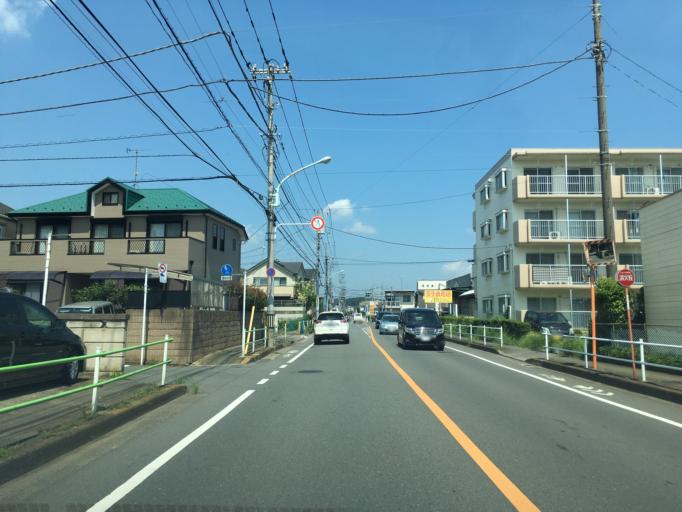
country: JP
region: Tokyo
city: Fussa
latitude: 35.7446
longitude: 139.3719
